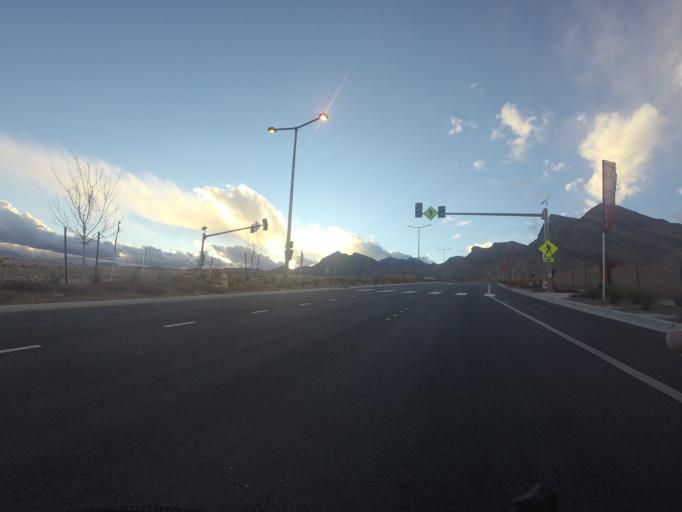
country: US
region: Nevada
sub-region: Clark County
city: Summerlin South
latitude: 36.2062
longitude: -115.3430
